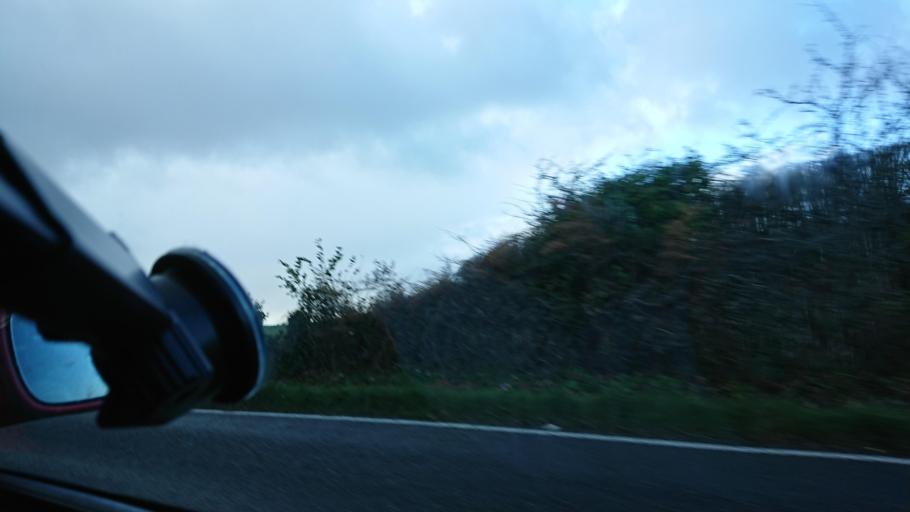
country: GB
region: England
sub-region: Cornwall
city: Looe
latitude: 50.3529
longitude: -4.4736
